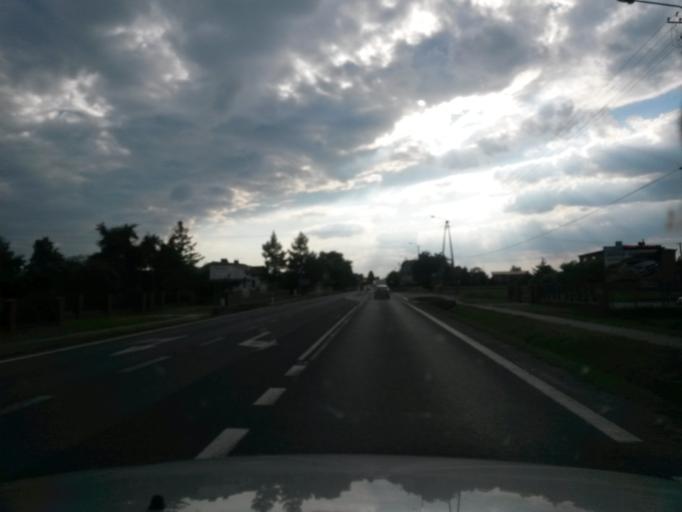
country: PL
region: Lodz Voivodeship
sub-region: Powiat piotrkowski
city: Wola Krzysztoporska
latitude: 51.4148
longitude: 19.5830
